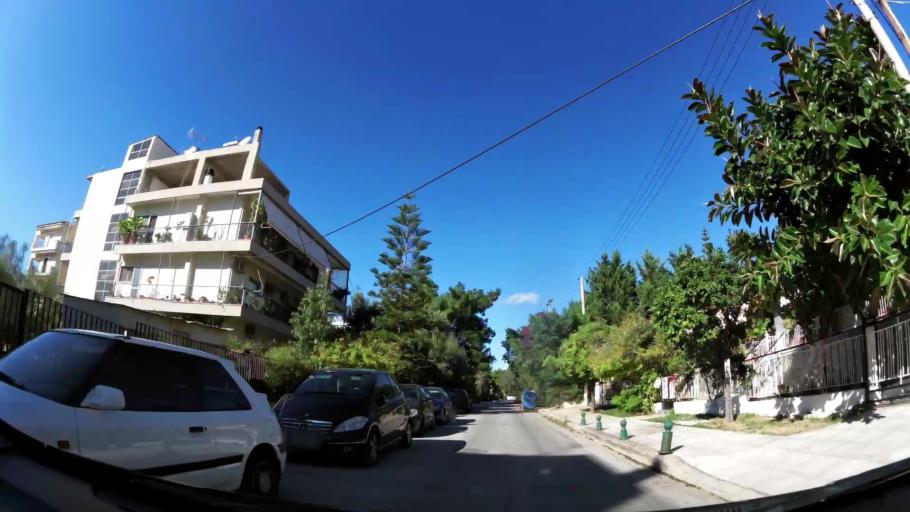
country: GR
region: Attica
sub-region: Nomarchia Athinas
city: Glyfada
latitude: 37.8515
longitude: 23.7571
